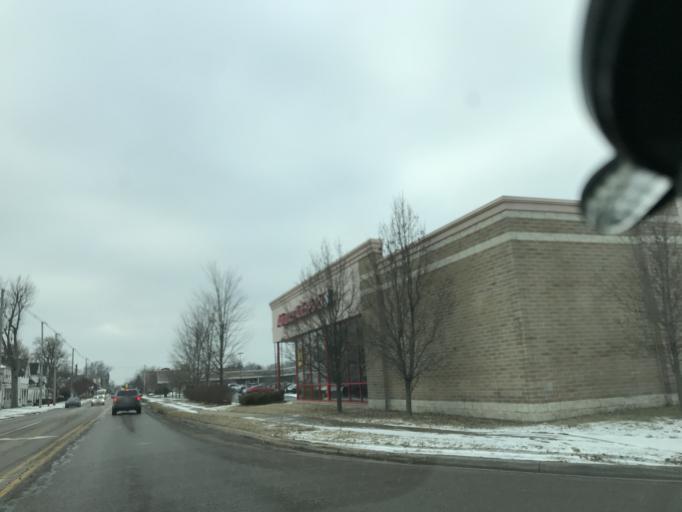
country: US
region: Michigan
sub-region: Ottawa County
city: Zeeland
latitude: 42.8139
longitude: -86.0191
